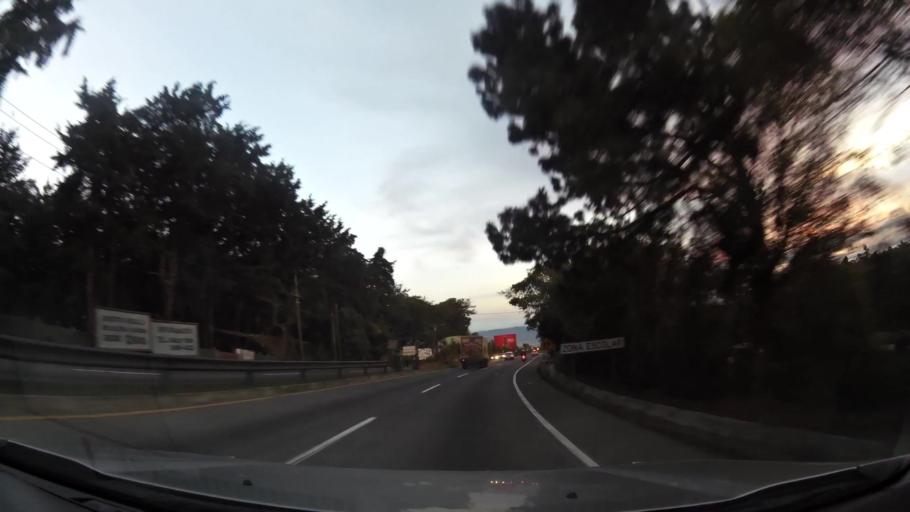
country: GT
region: Guatemala
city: Mixco
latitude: 14.6160
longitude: -90.6196
